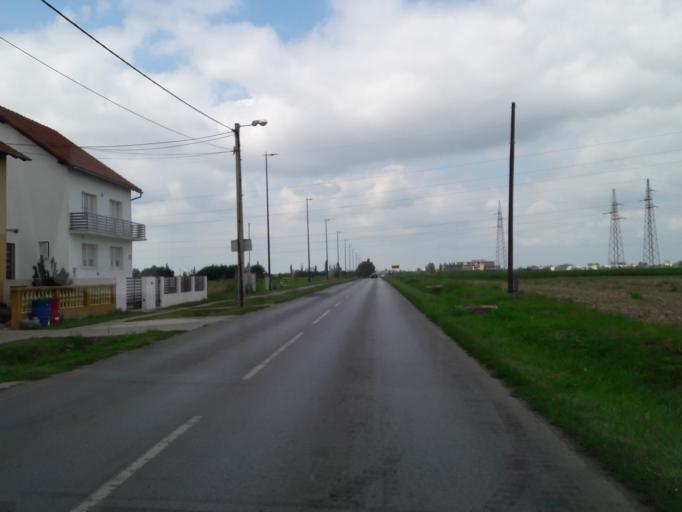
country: HR
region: Osjecko-Baranjska
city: Tenja
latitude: 45.5215
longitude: 18.7269
